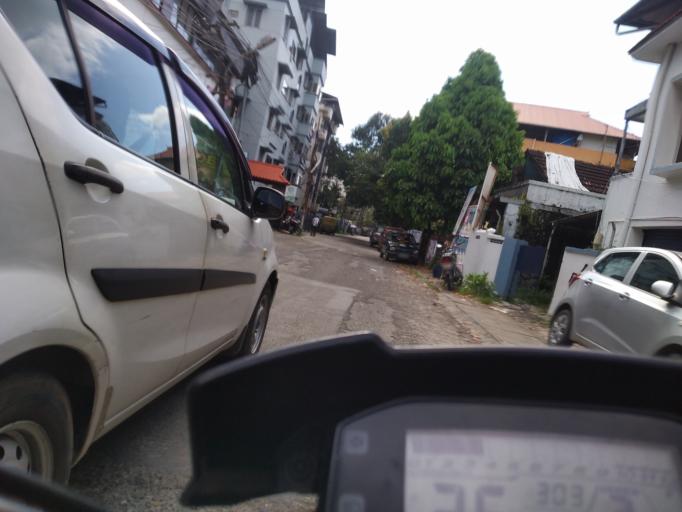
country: IN
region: Kerala
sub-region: Ernakulam
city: Cochin
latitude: 9.9846
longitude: 76.2848
